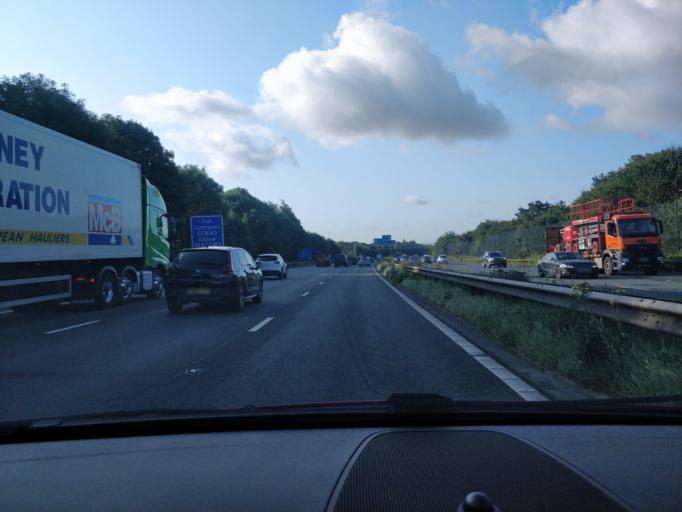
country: GB
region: England
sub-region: Knowsley
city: Prescot
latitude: 53.4242
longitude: -2.8167
